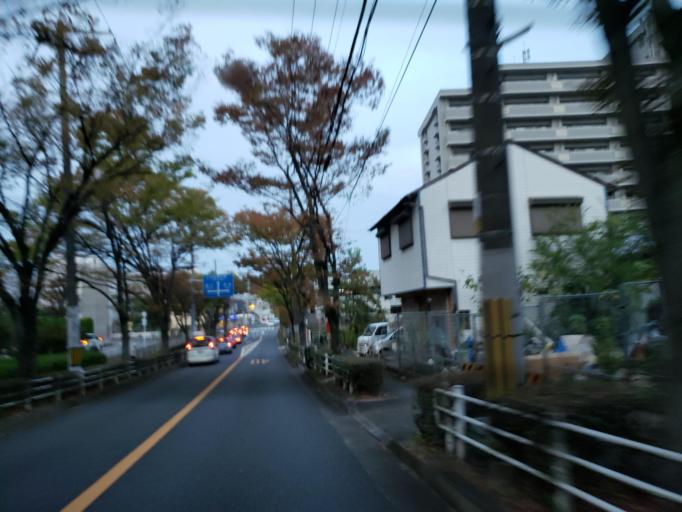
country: JP
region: Osaka
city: Suita
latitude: 34.7939
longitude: 135.5285
